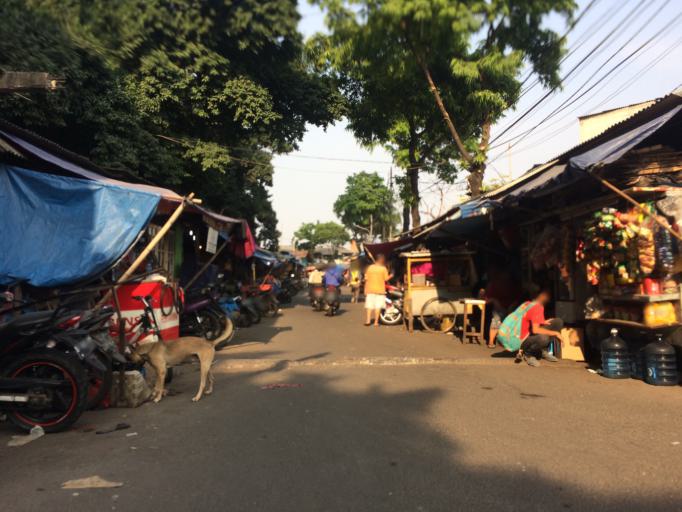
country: ID
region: Jakarta Raya
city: Jakarta
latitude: -6.2083
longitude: 106.8405
